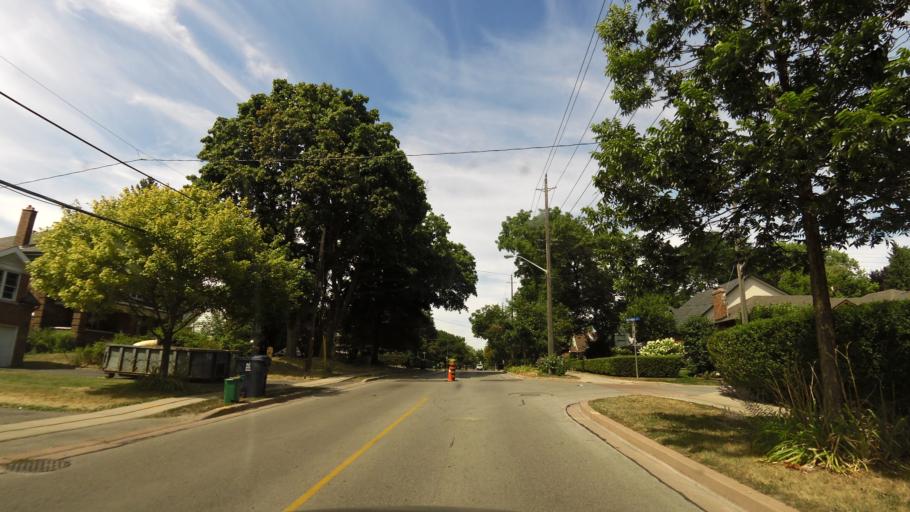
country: CA
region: Ontario
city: Etobicoke
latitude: 43.6359
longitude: -79.5000
